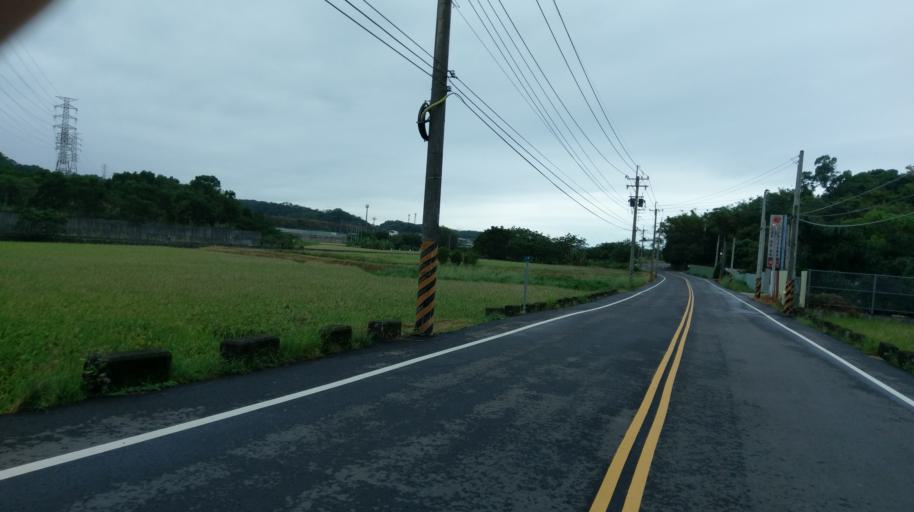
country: TW
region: Taiwan
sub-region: Hsinchu
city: Hsinchu
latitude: 24.7301
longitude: 120.9475
